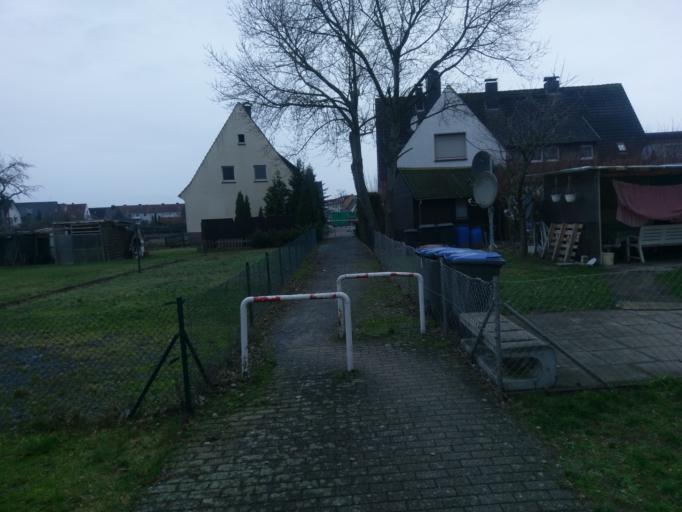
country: DE
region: North Rhine-Westphalia
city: Oelde
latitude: 51.8339
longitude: 8.1604
